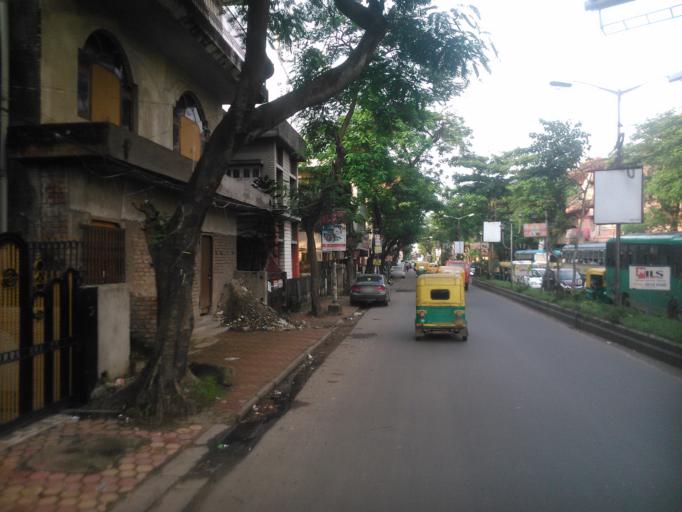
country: IN
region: West Bengal
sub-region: North 24 Parganas
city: Garui
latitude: 22.5902
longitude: 88.3973
